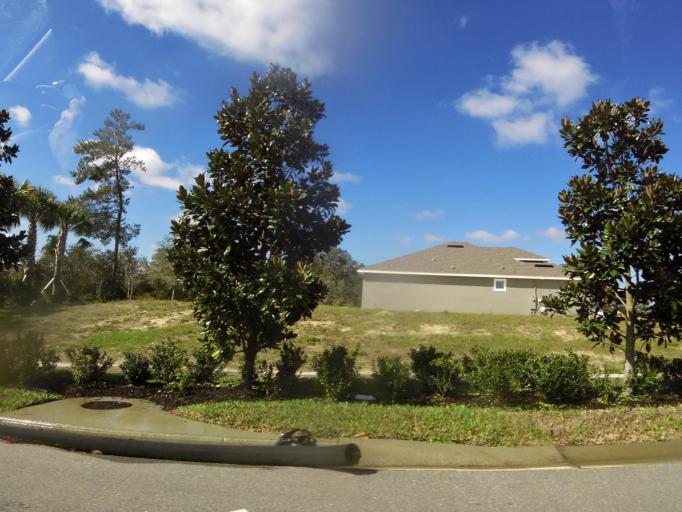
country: US
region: Florida
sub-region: Volusia County
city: Orange City
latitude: 28.9344
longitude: -81.3107
